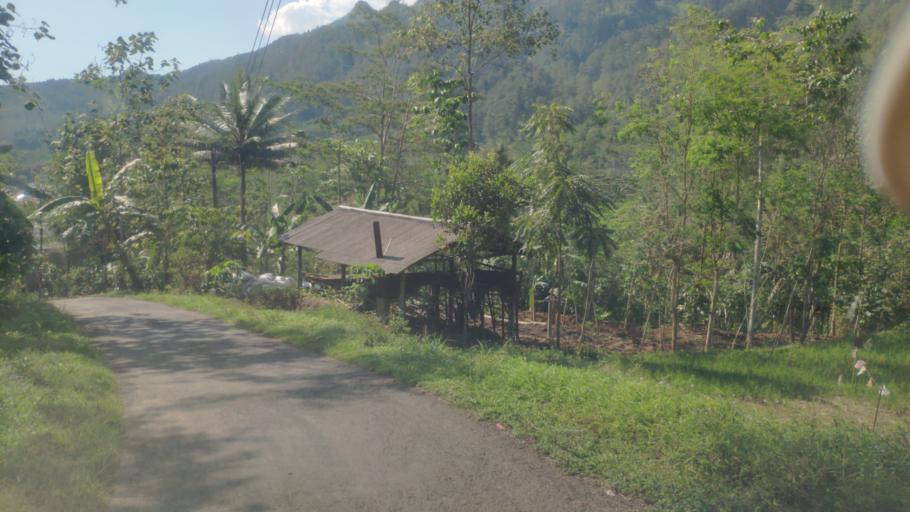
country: ID
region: Central Java
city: Buaran
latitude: -7.2245
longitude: 109.5969
